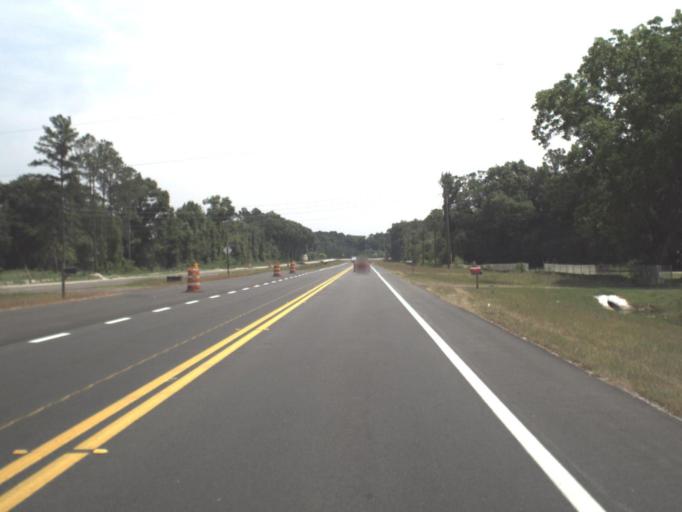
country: US
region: Florida
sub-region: Nassau County
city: Callahan
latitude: 30.5503
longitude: -81.8437
